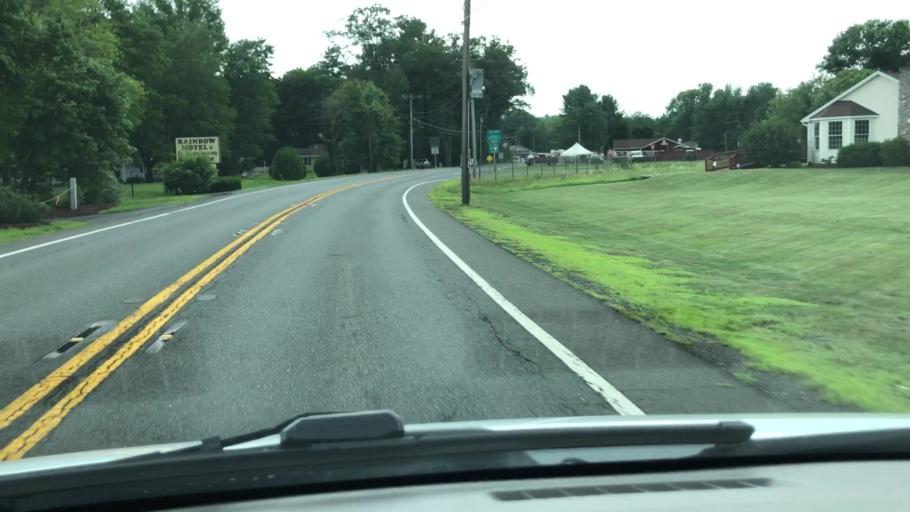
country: US
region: Massachusetts
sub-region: Franklin County
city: Whately
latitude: 42.4250
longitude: -72.6217
